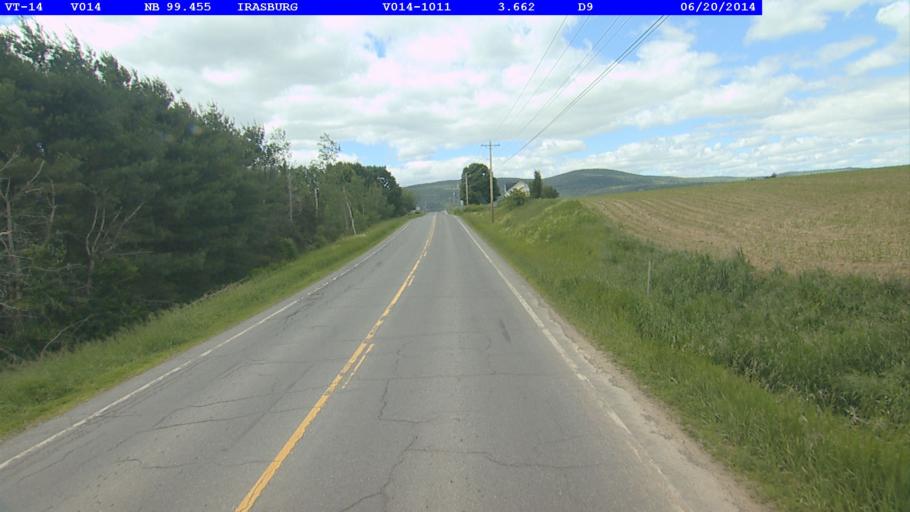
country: US
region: Vermont
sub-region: Orleans County
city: Newport
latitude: 44.8137
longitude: -72.2920
